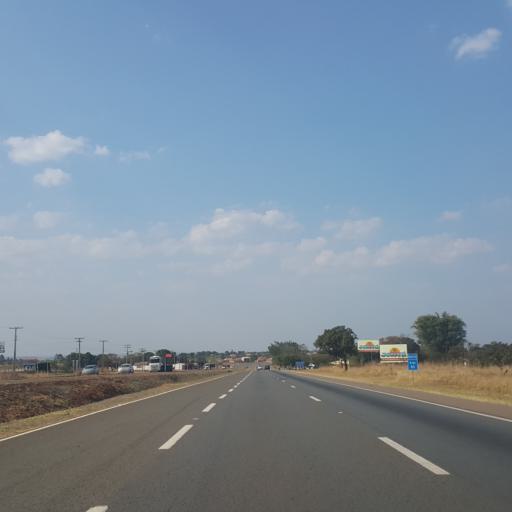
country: BR
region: Goias
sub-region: Abadiania
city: Abadiania
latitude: -16.1936
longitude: -48.7279
